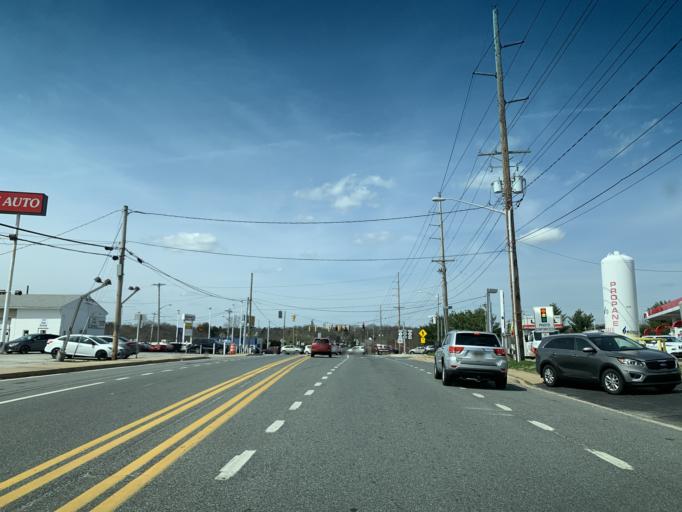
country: US
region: Delaware
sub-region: New Castle County
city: Newport
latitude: 39.7354
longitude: -75.6298
